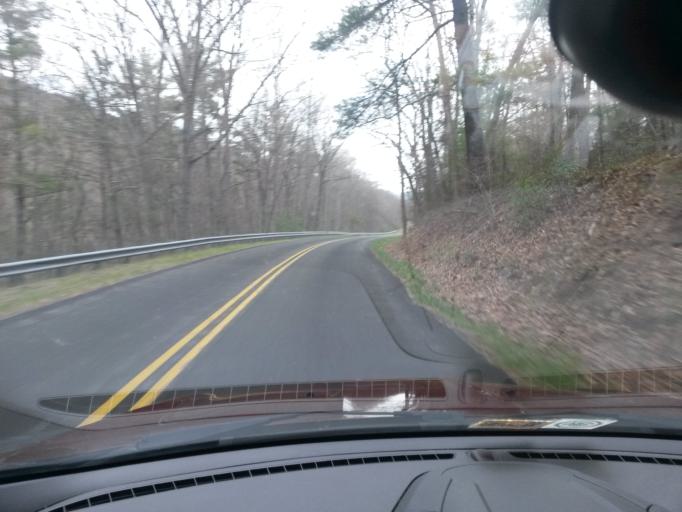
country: US
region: Virginia
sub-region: Alleghany County
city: Clifton Forge
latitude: 37.8218
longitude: -79.6652
